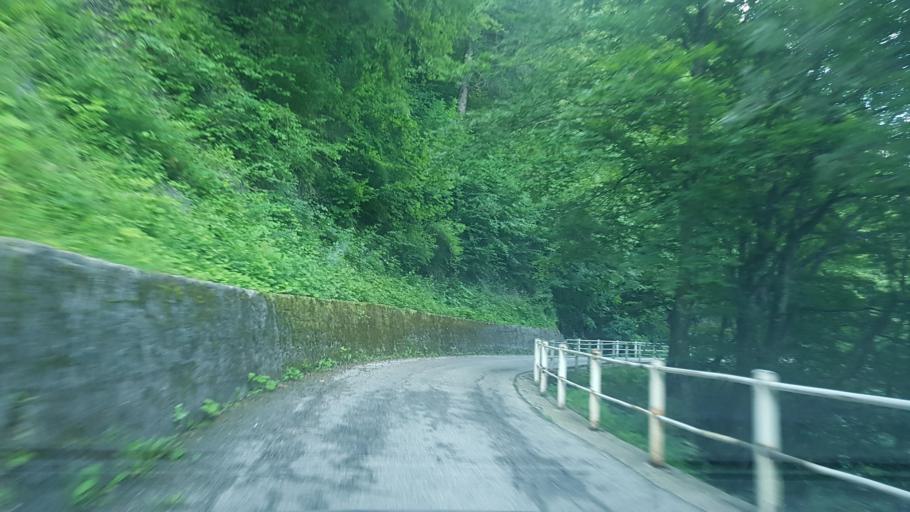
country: IT
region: Friuli Venezia Giulia
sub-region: Provincia di Udine
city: Paularo
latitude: 46.4845
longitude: 13.0982
